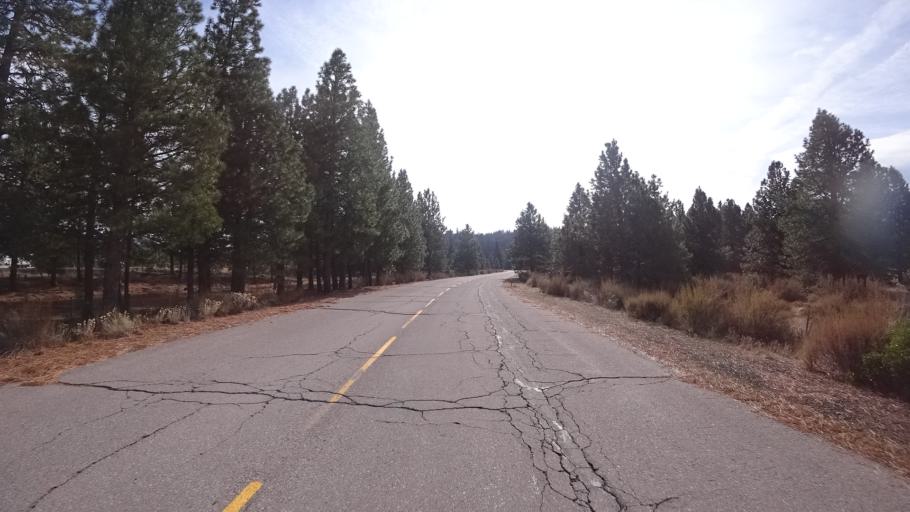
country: US
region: California
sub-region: Siskiyou County
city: Weed
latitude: 41.3989
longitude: -122.3834
